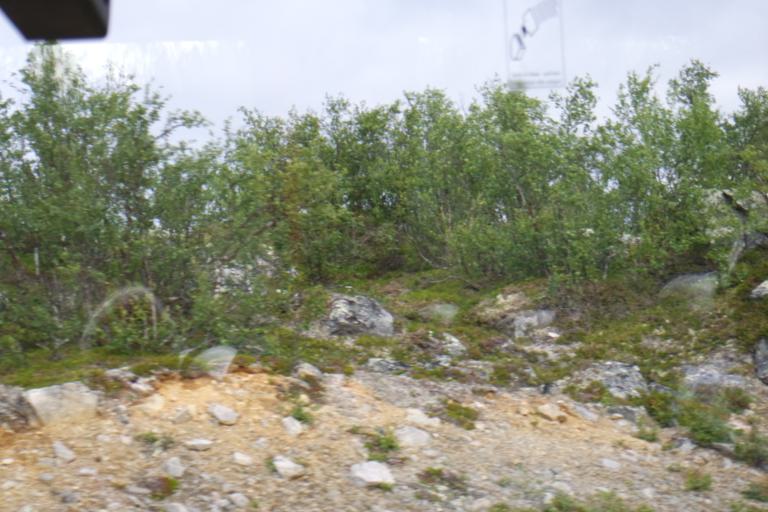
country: NO
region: Finnmark Fylke
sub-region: Karasjok
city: Karasjohka
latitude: 69.7453
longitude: 25.2262
